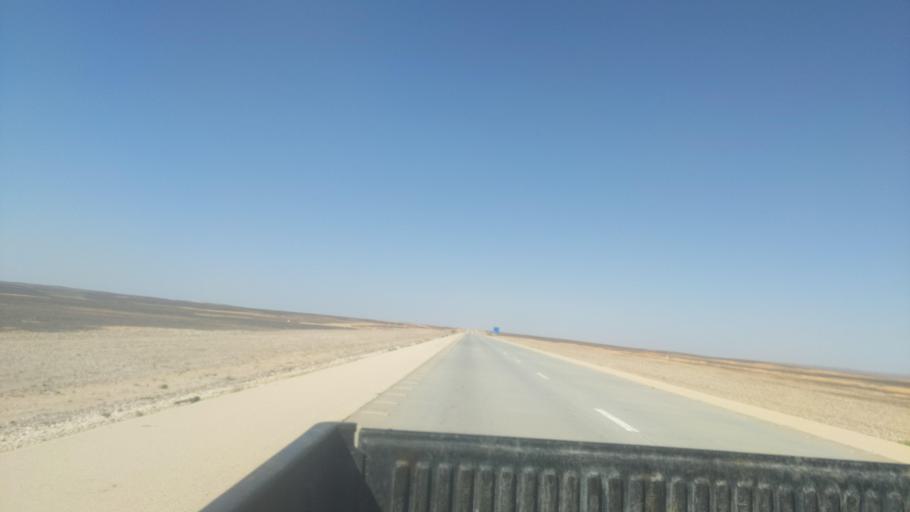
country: JO
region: Amman
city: Al Azraq ash Shamali
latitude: 31.4431
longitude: 36.7577
